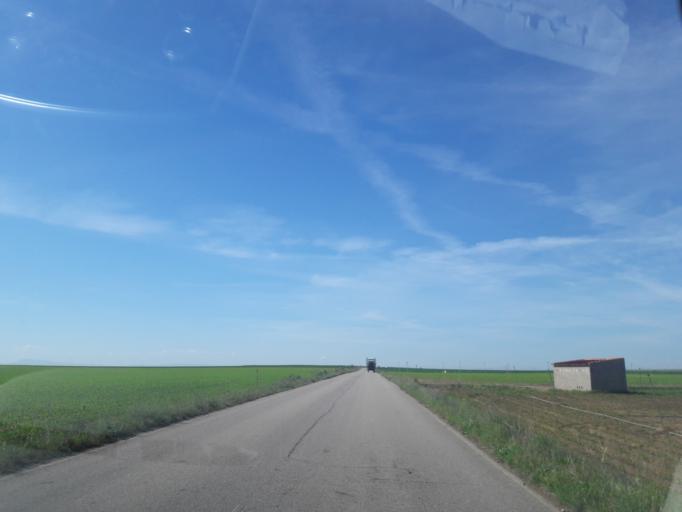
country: ES
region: Castille and Leon
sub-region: Provincia de Salamanca
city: Villoruela
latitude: 41.0232
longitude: -5.3923
